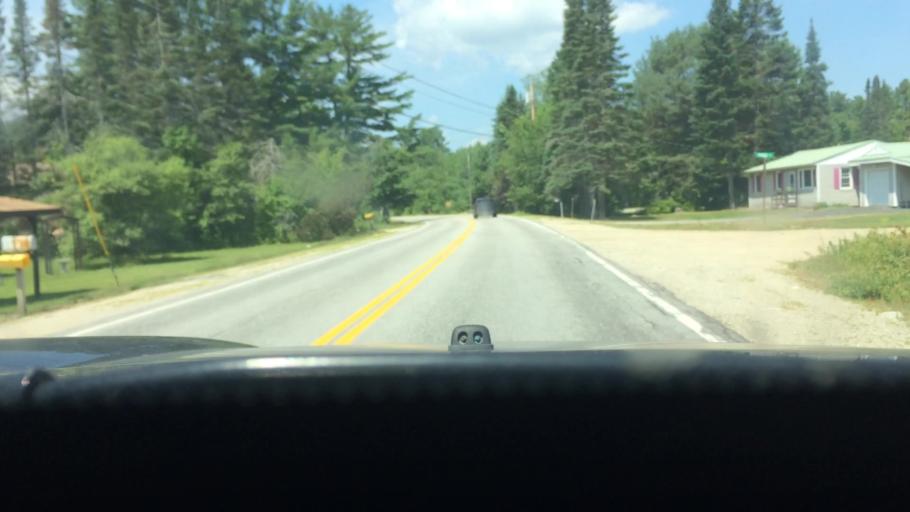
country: US
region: Maine
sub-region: Oxford County
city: Oxford
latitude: 44.1342
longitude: -70.4532
